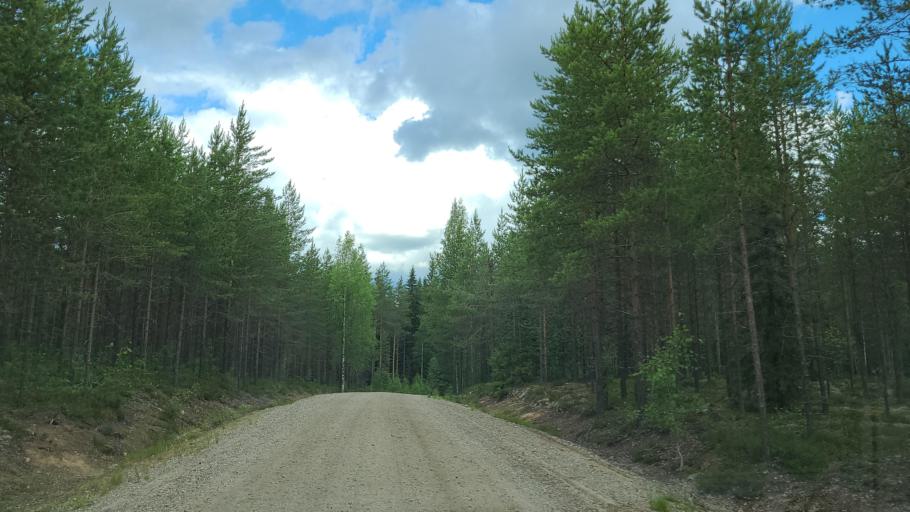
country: FI
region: Northern Savo
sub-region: Koillis-Savo
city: Kaavi
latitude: 63.0481
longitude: 28.8164
